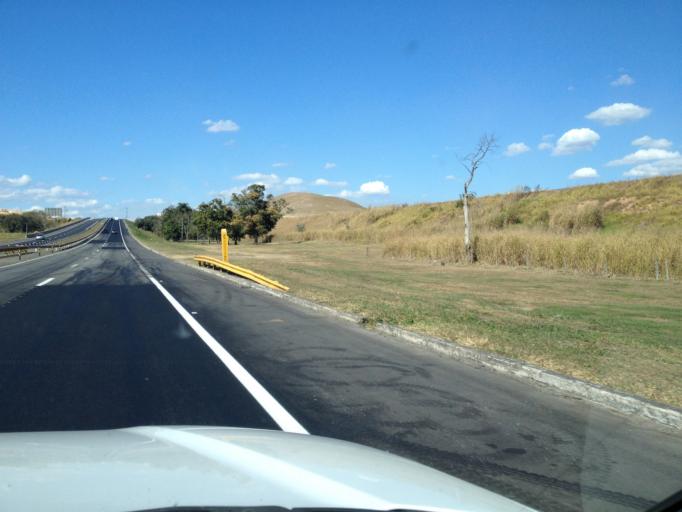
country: BR
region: Rio de Janeiro
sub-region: Porto Real
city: Porto Real
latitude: -22.4505
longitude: -44.3346
